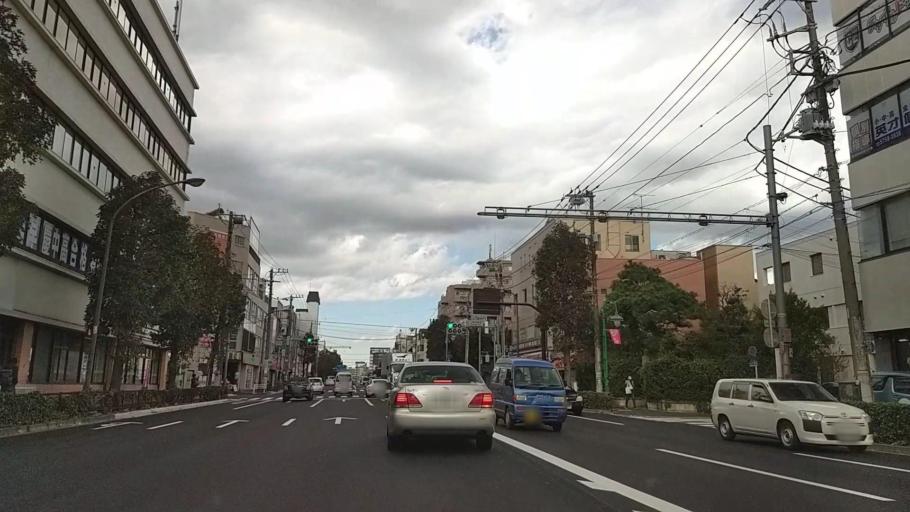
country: JP
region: Tokyo
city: Tokyo
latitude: 35.6113
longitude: 139.6385
